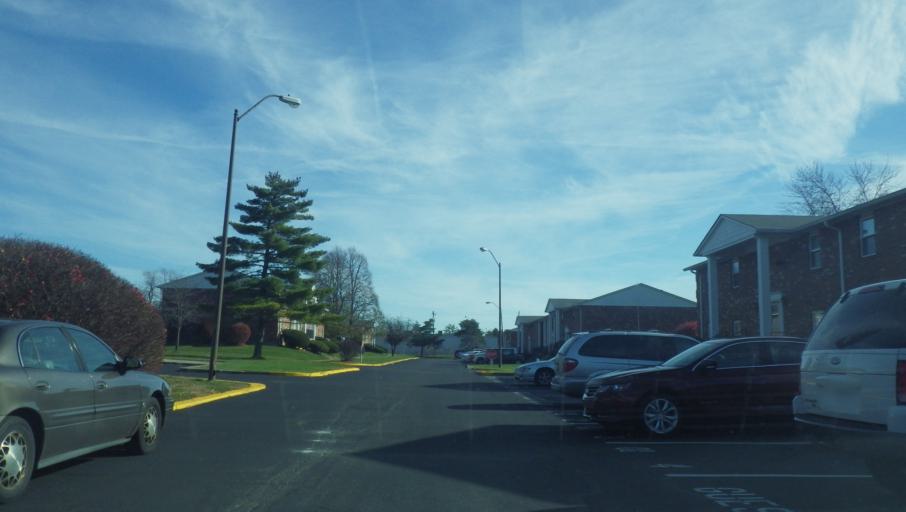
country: US
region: Indiana
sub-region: Marion County
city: Cumberland
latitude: 39.7985
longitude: -85.9949
